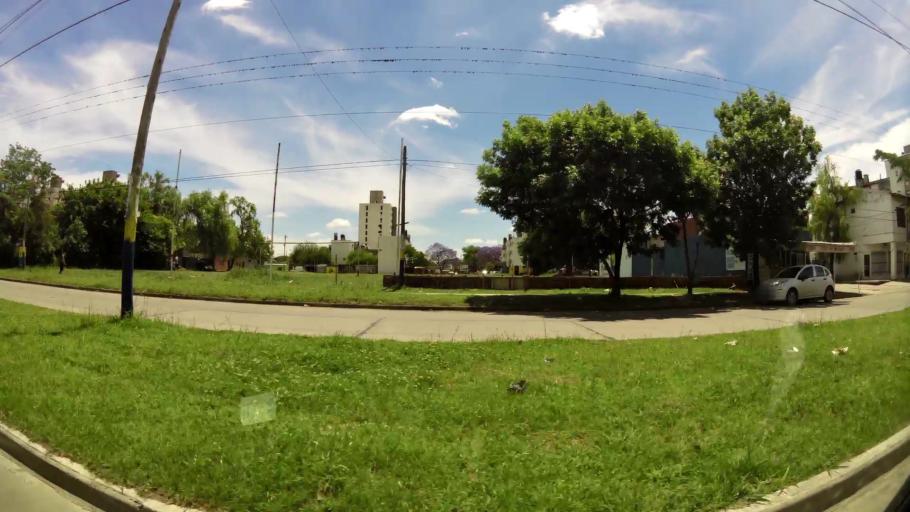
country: AR
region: Santa Fe
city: Gobernador Galvez
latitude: -32.9933
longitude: -60.6240
